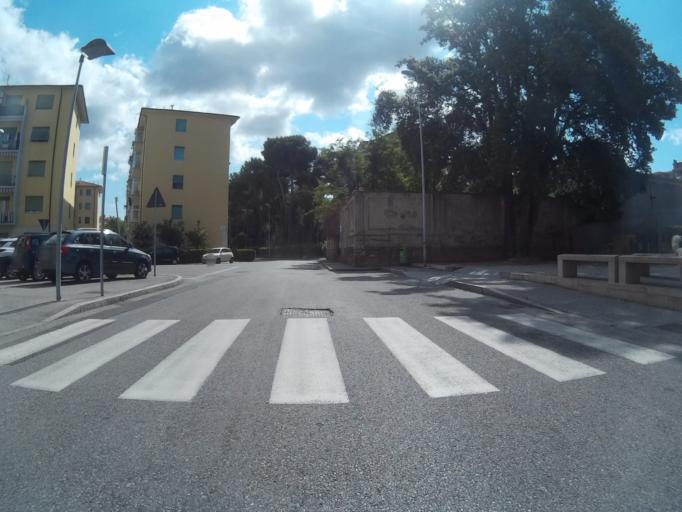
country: IT
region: Tuscany
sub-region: Provincia di Livorno
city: Livorno
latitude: 43.5635
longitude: 10.3212
